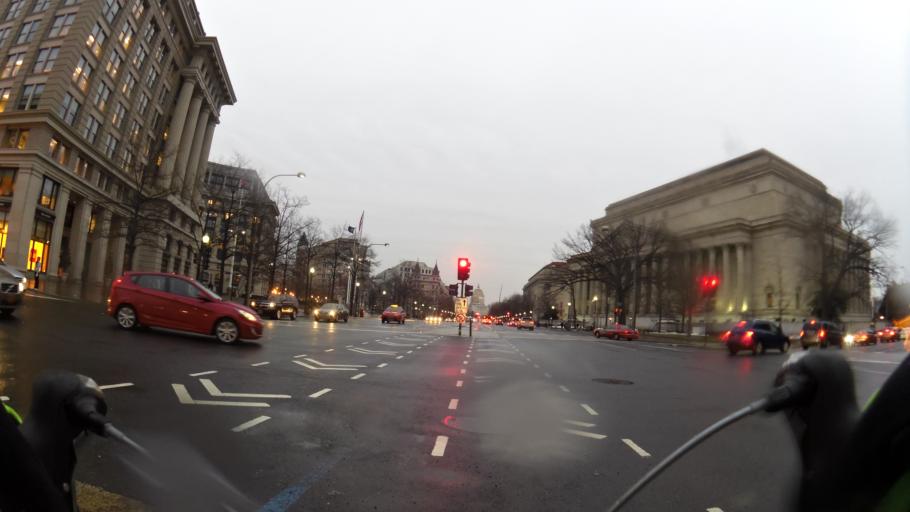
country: US
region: Washington, D.C.
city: Washington, D.C.
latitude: 38.8939
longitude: -77.0241
